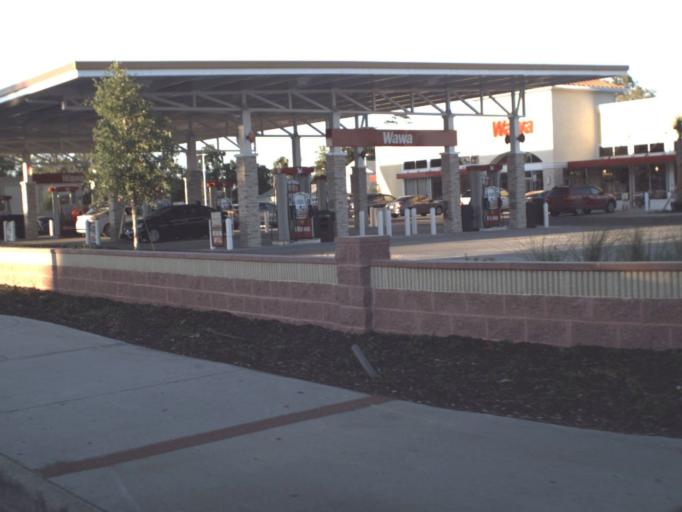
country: US
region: Florida
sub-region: Orange County
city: Azalea Park
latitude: 28.5277
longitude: -81.3103
